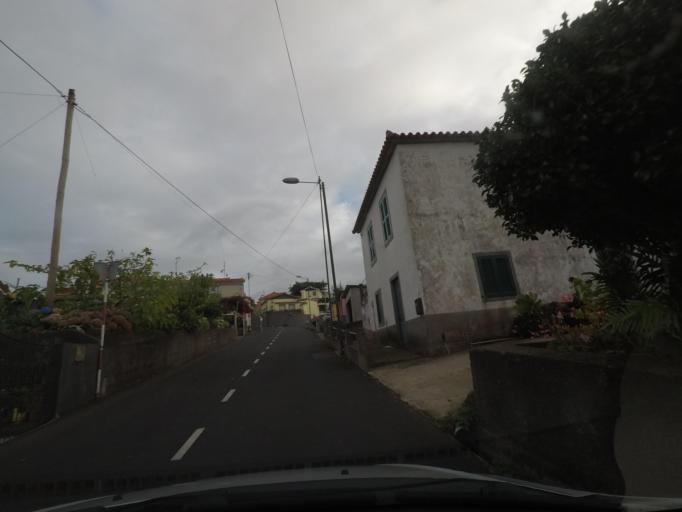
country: PT
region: Madeira
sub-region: Santana
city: Santana
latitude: 32.8074
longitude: -16.8766
